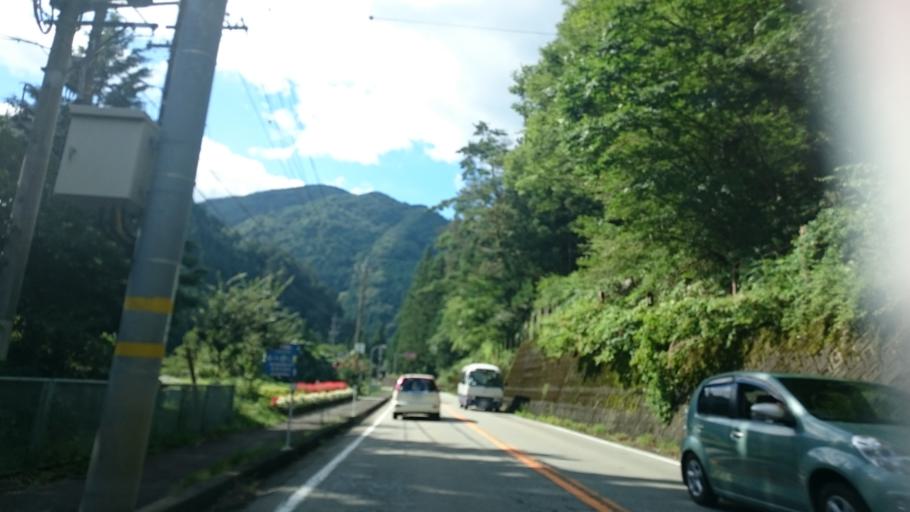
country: JP
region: Gifu
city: Gujo
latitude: 35.7747
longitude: 137.2544
